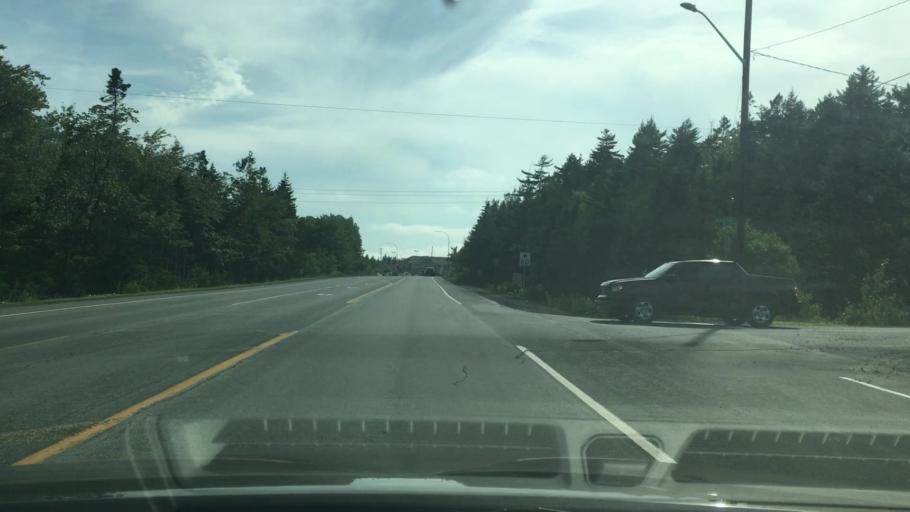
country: CA
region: Nova Scotia
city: Dartmouth
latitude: 44.7061
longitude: -63.8522
